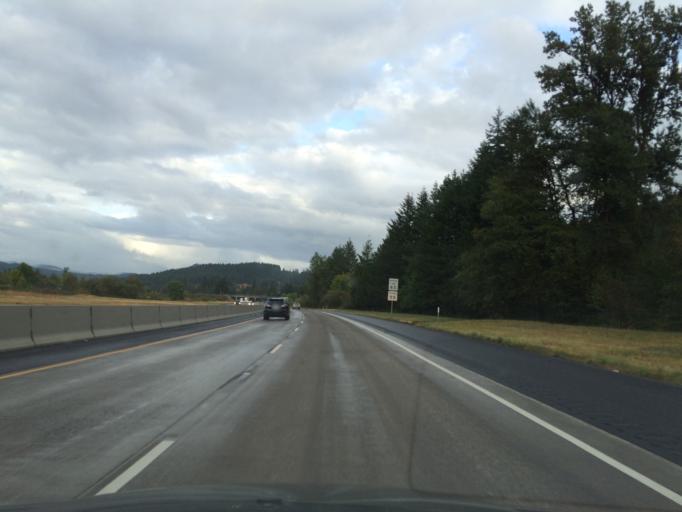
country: US
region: Oregon
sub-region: Lane County
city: Cottage Grove
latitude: 43.7499
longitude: -123.1223
